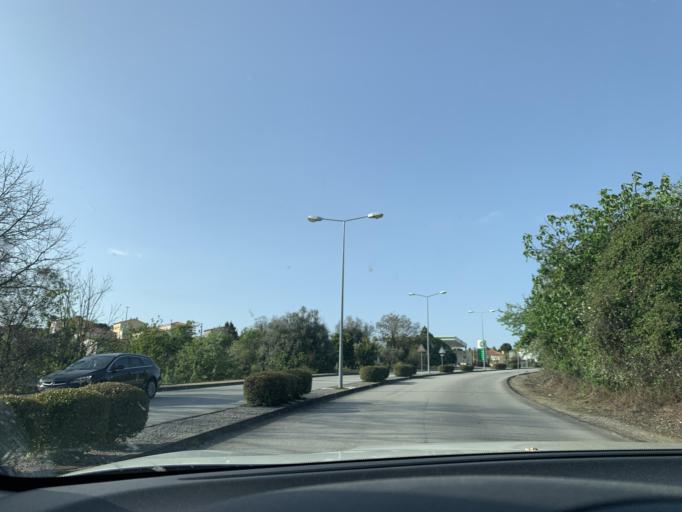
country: PT
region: Viseu
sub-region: Mangualde
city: Mangualde
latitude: 40.5878
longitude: -7.7644
